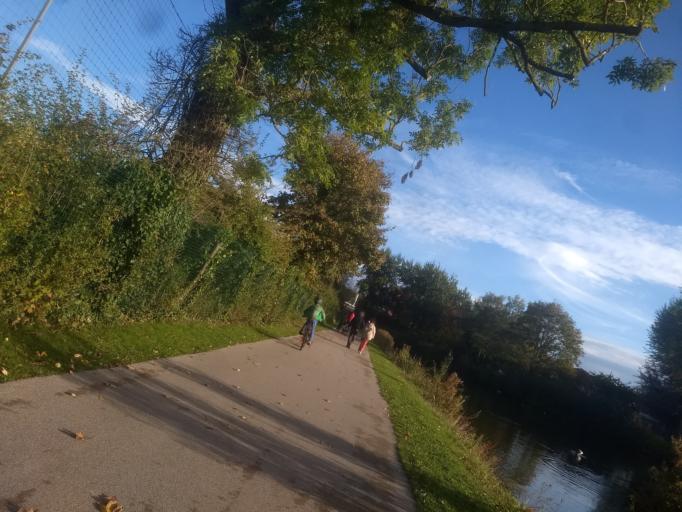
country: FR
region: Nord-Pas-de-Calais
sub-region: Departement du Pas-de-Calais
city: Saint-Laurent-Blangy
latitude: 50.2991
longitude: 2.7974
